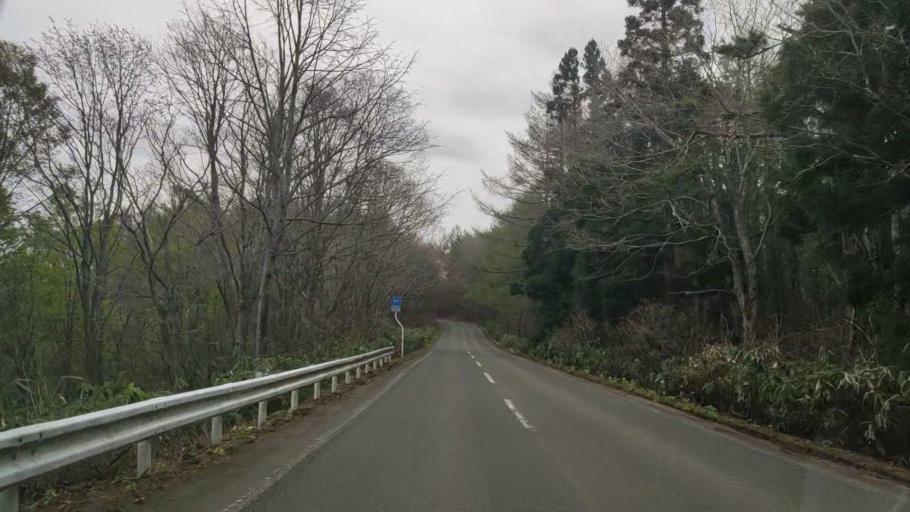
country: JP
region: Aomori
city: Aomori Shi
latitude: 40.7255
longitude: 140.8491
